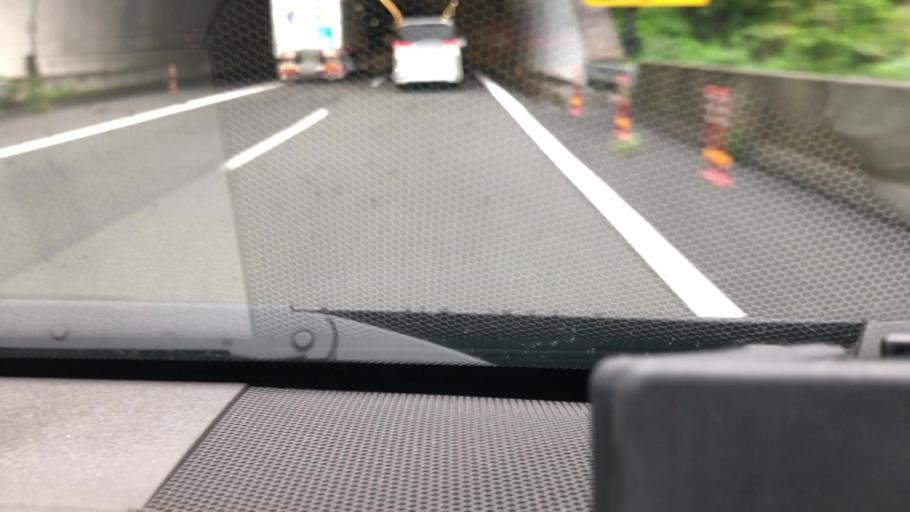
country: JP
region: Shizuoka
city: Shizuoka-shi
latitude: 35.0470
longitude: 138.4099
